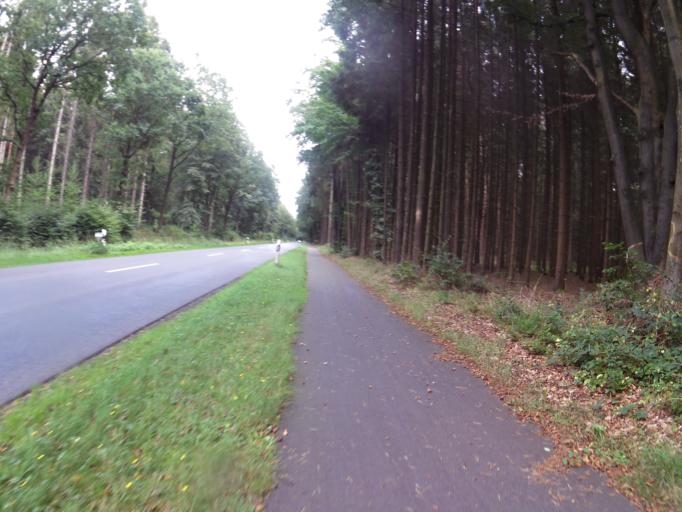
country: DE
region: Lower Saxony
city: Hipstedt
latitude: 53.5004
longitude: 8.9969
